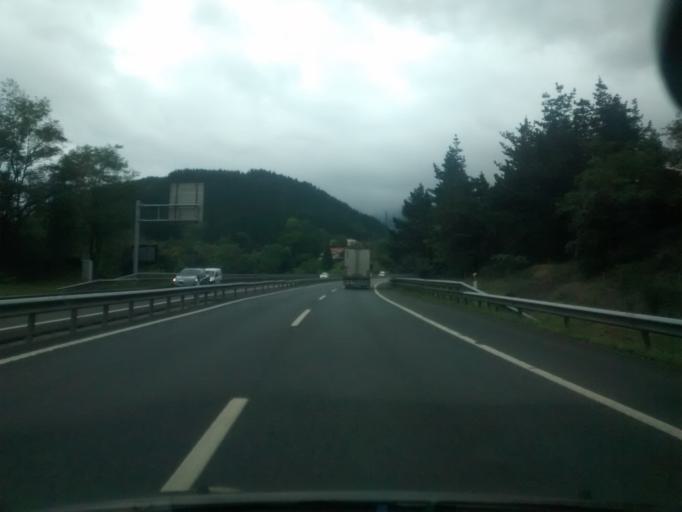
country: ES
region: Basque Country
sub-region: Provincia de Guipuzcoa
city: Elgoibar
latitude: 43.2298
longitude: -2.4034
